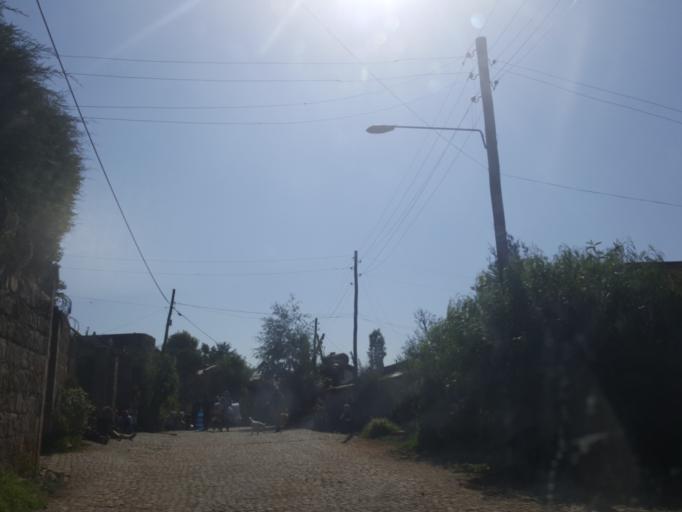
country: ET
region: Adis Abeba
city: Addis Ababa
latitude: 9.0486
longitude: 38.7344
